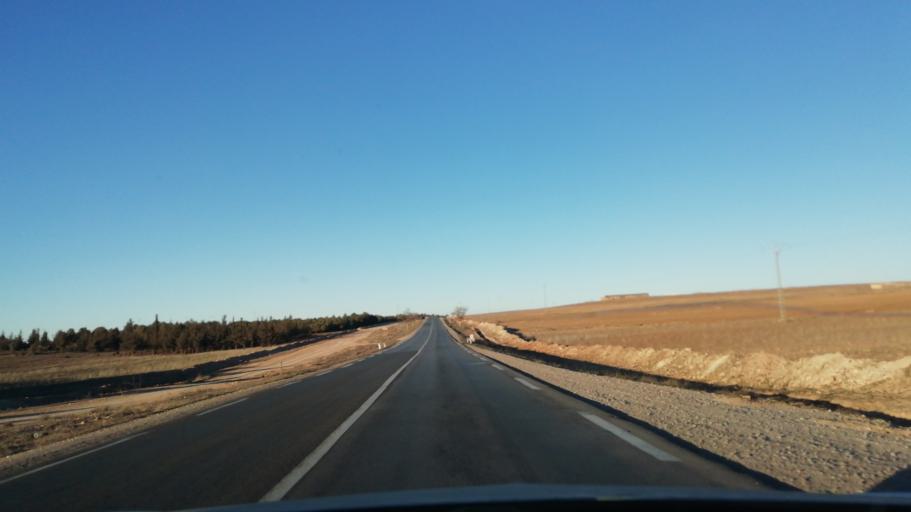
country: DZ
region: Saida
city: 'Ain el Hadjar
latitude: 34.5566
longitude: 0.1181
